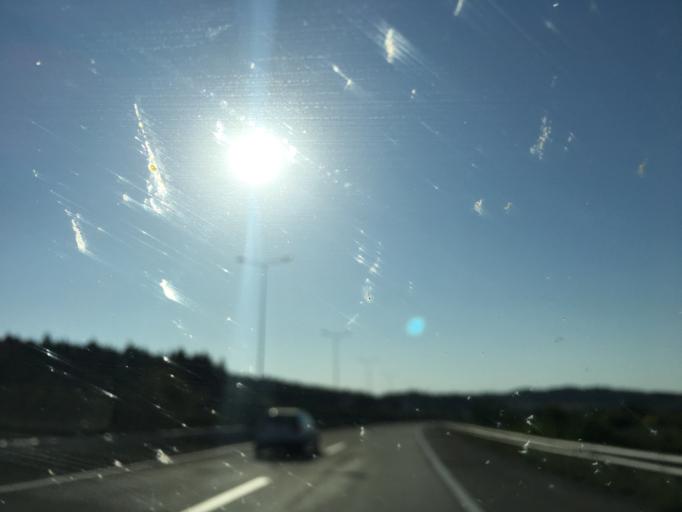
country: MK
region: Gevgelija
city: Gevgelija
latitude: 41.1485
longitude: 22.5237
